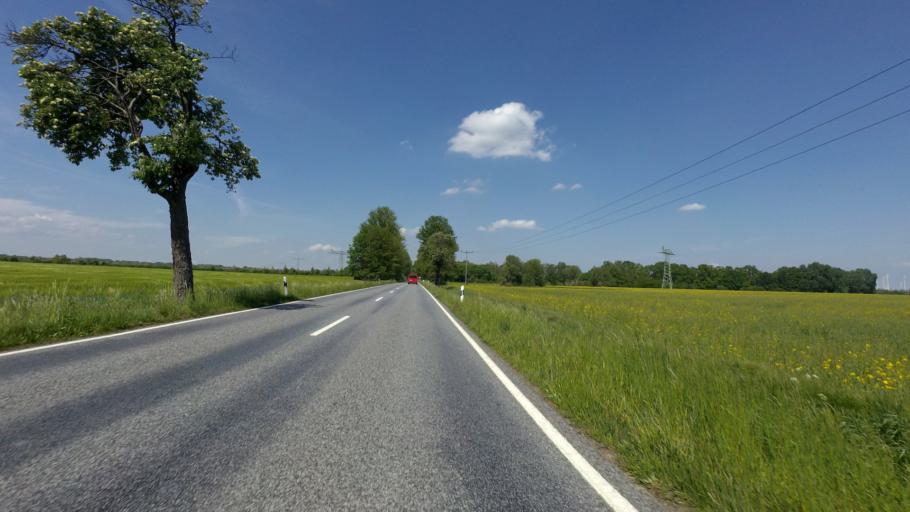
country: DE
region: Brandenburg
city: Luckau
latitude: 51.8391
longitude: 13.7555
